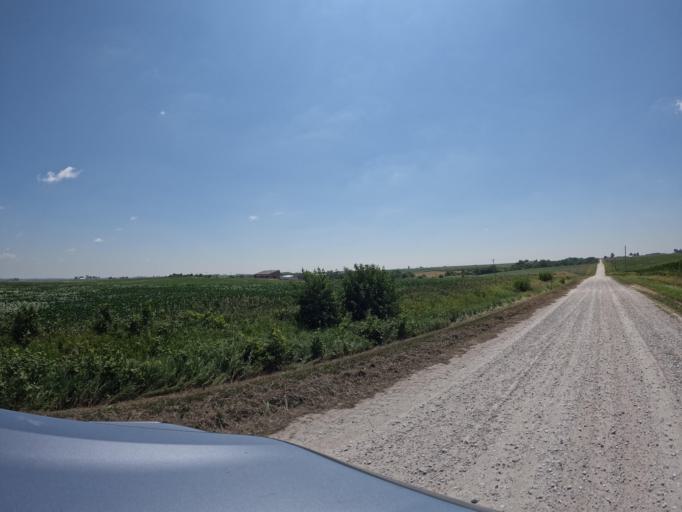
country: US
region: Iowa
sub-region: Keokuk County
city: Sigourney
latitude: 41.2805
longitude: -92.2381
